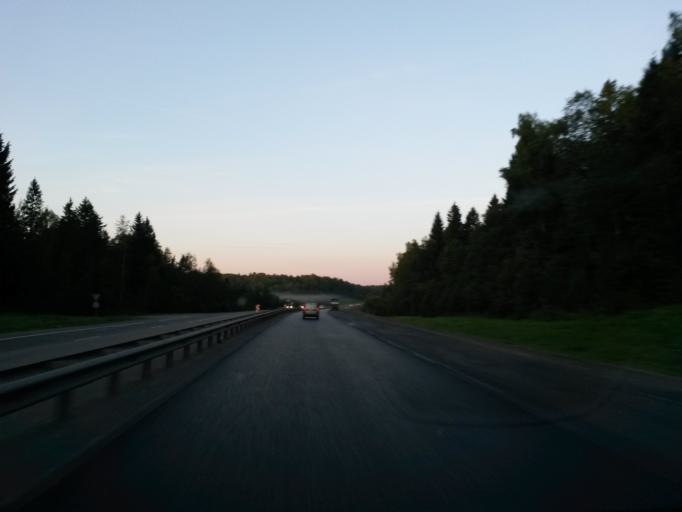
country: RU
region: Moskovskaya
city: Svatkovo
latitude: 56.3006
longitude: 38.2358
